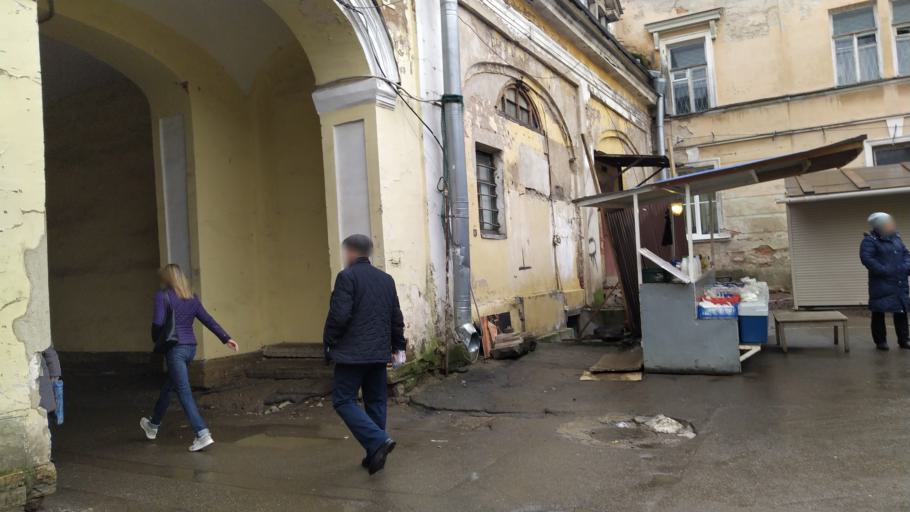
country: RU
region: St.-Petersburg
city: Pushkin
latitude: 59.7190
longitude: 30.4071
